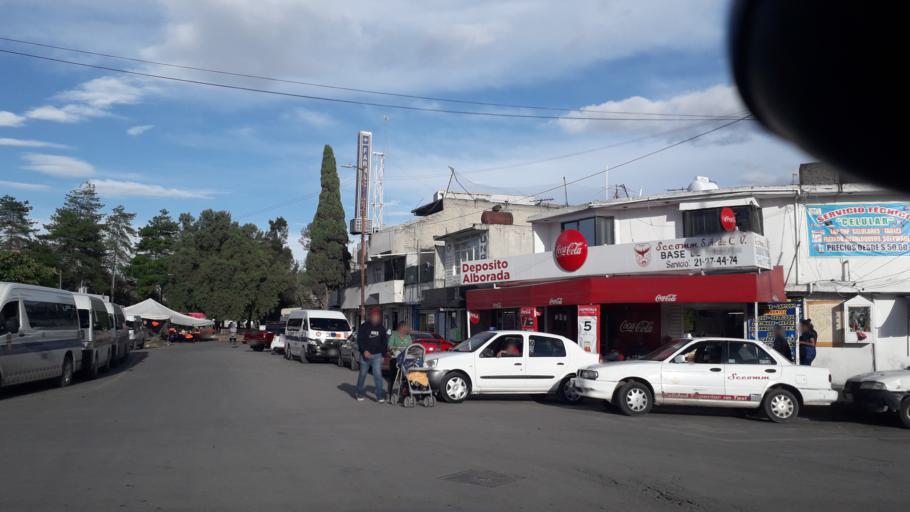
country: MX
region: Mexico
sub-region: Jaltenco
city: Alborada Jaltenco
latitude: 19.6611
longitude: -99.0707
